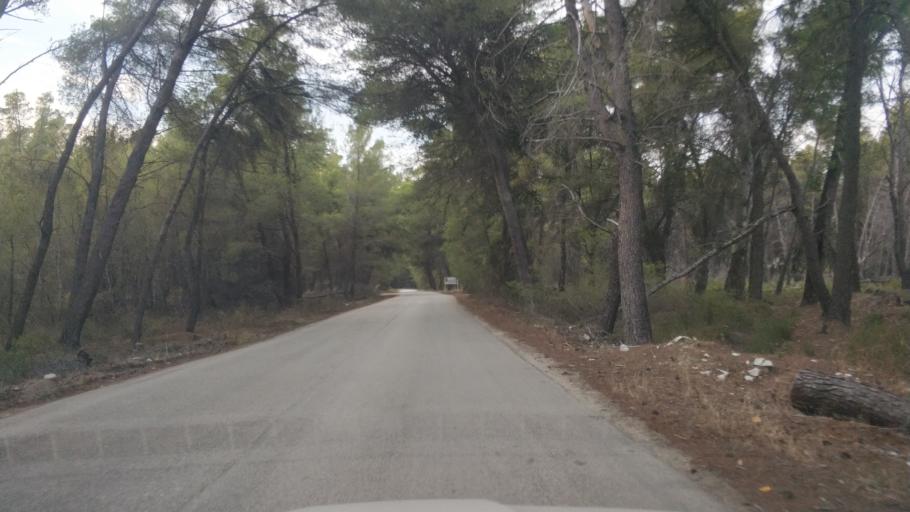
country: AL
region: Vlore
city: Vlore
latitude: 40.4839
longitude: 19.4469
